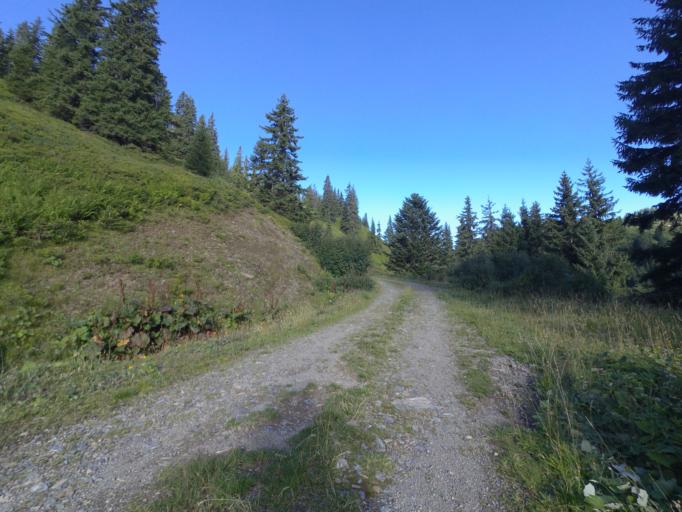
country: AT
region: Salzburg
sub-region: Politischer Bezirk Sankt Johann im Pongau
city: Goldegg
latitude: 47.3536
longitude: 13.0773
